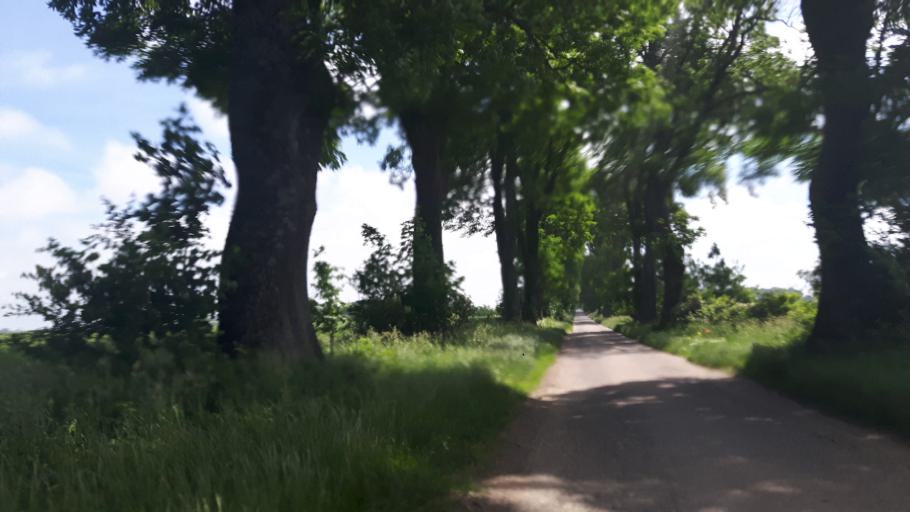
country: PL
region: West Pomeranian Voivodeship
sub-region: Powiat slawienski
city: Darlowo
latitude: 54.4704
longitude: 16.4754
